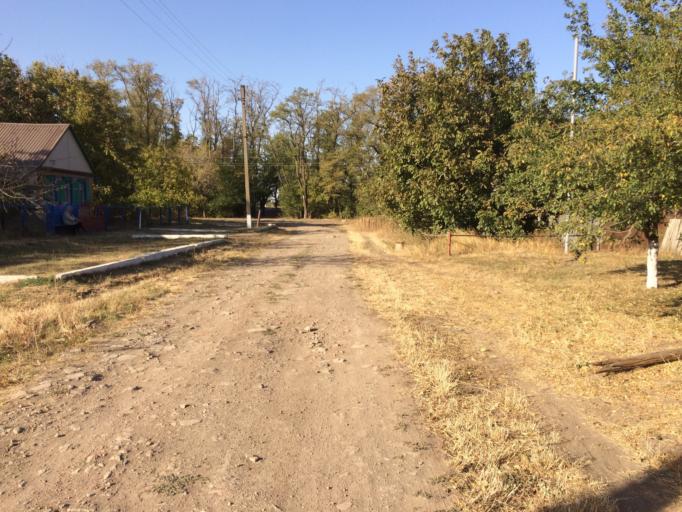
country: RU
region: Rostov
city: Gigant
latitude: 46.5267
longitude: 41.1882
